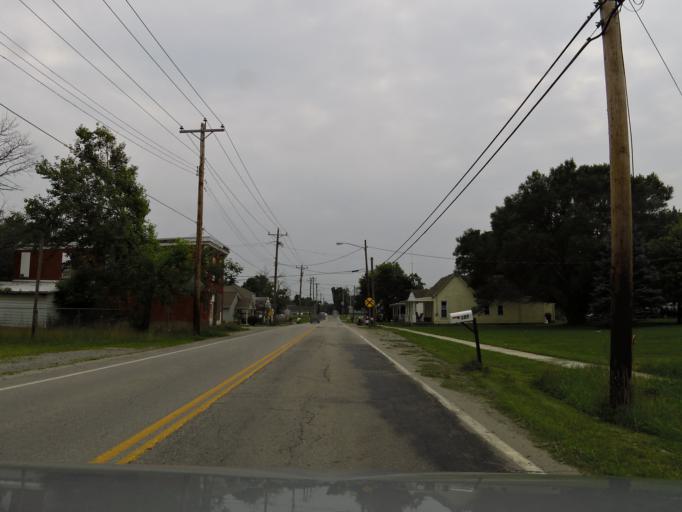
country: US
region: Ohio
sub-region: Clinton County
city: Blanchester
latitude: 39.3056
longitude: -83.9105
